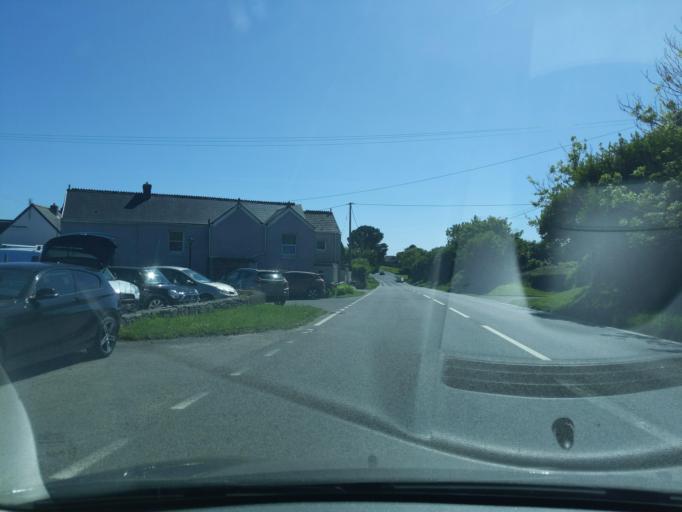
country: GB
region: England
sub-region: Cornwall
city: Wendron
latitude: 50.1237
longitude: -5.2376
